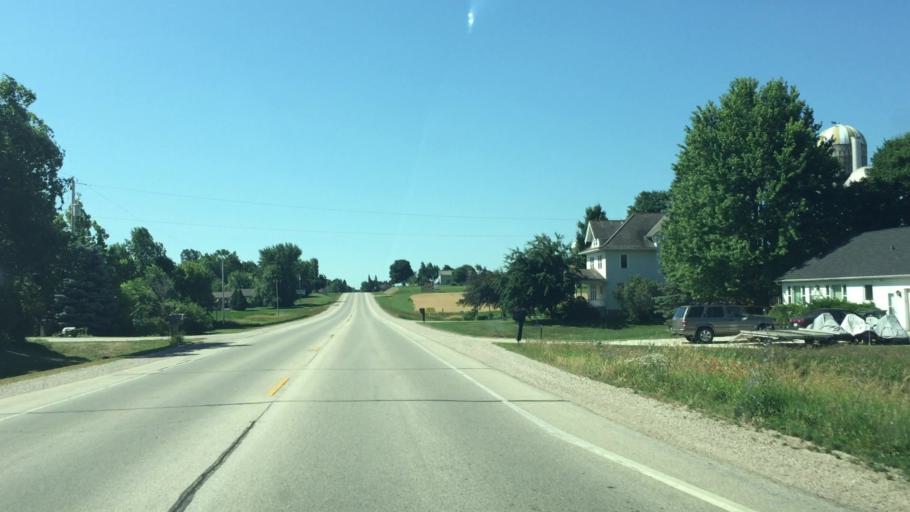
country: US
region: Wisconsin
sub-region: Calumet County
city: Chilton
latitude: 44.0510
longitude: -88.1630
